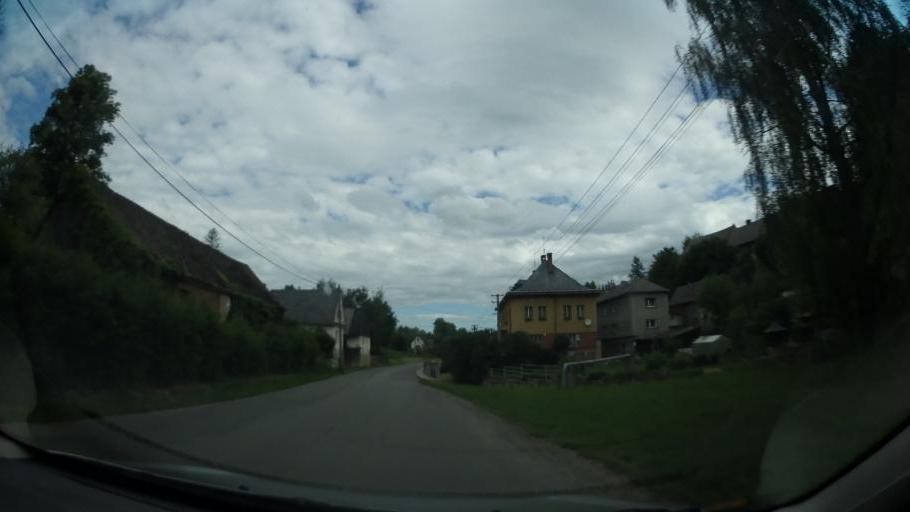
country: CZ
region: Pardubicky
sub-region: Okres Svitavy
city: Moravska Trebova
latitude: 49.8257
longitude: 16.7032
